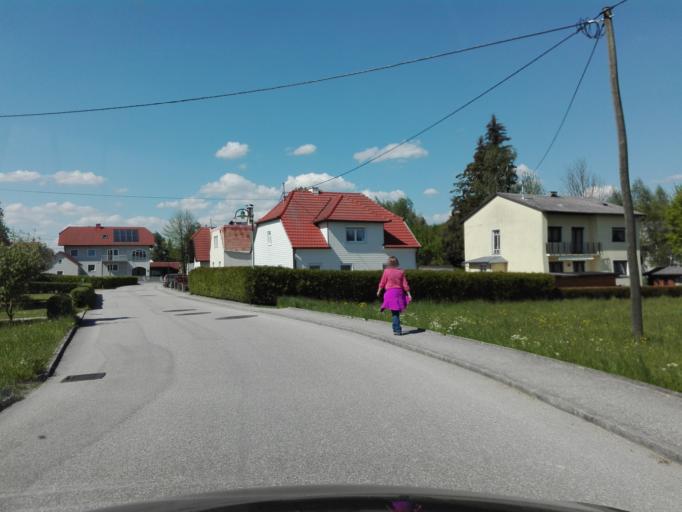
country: AT
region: Upper Austria
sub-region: Politischer Bezirk Grieskirchen
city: Bad Schallerbach
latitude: 48.3169
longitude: 13.9009
